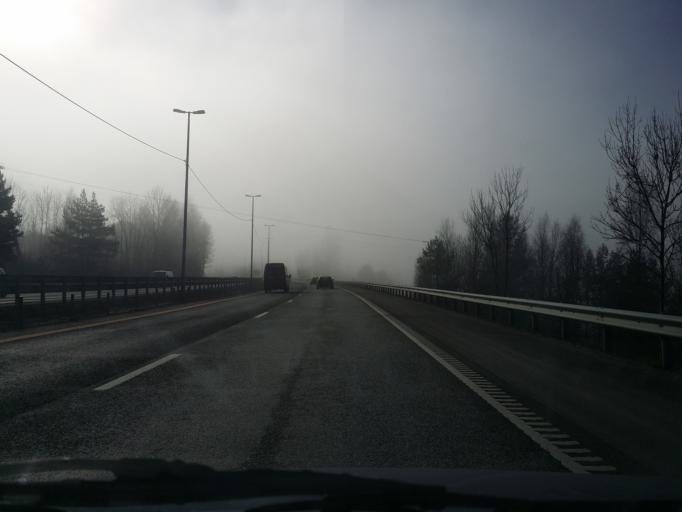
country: NO
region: Buskerud
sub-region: Lier
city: Tranby
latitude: 59.7856
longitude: 10.2728
